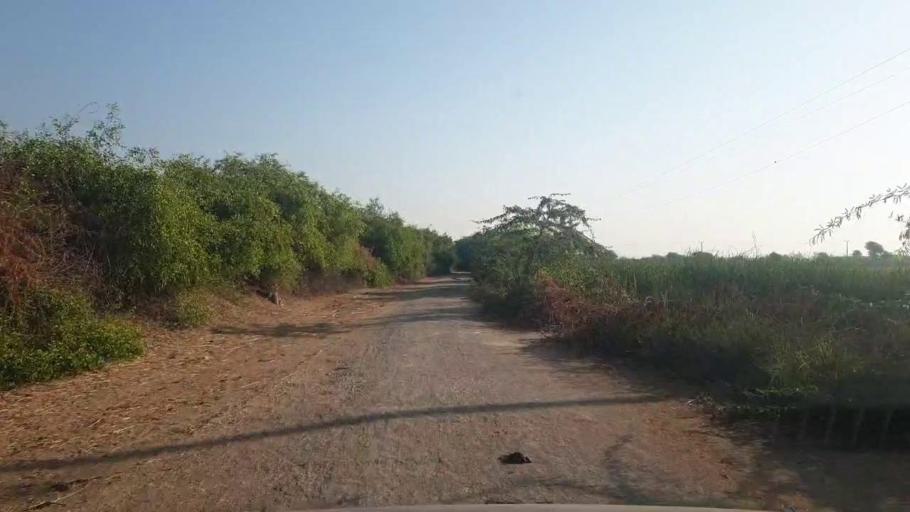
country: PK
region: Sindh
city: Badin
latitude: 24.7359
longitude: 68.8847
